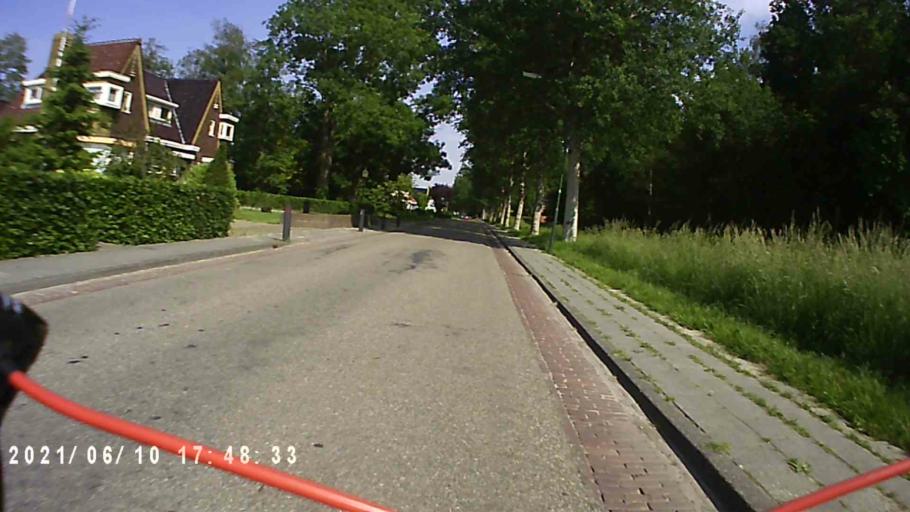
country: NL
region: Groningen
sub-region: Gemeente De Marne
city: Ulrum
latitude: 53.3369
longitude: 6.3081
